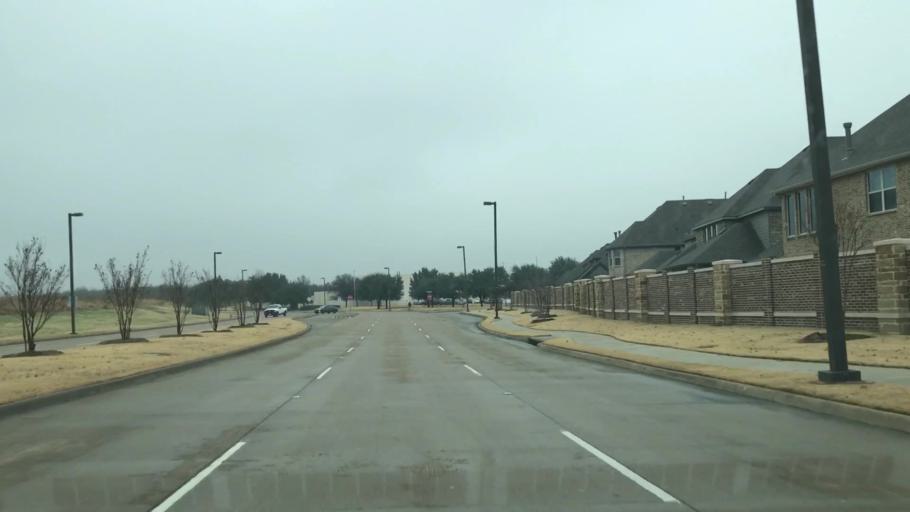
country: US
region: Texas
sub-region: Dallas County
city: Farmers Branch
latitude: 32.8847
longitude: -96.9404
